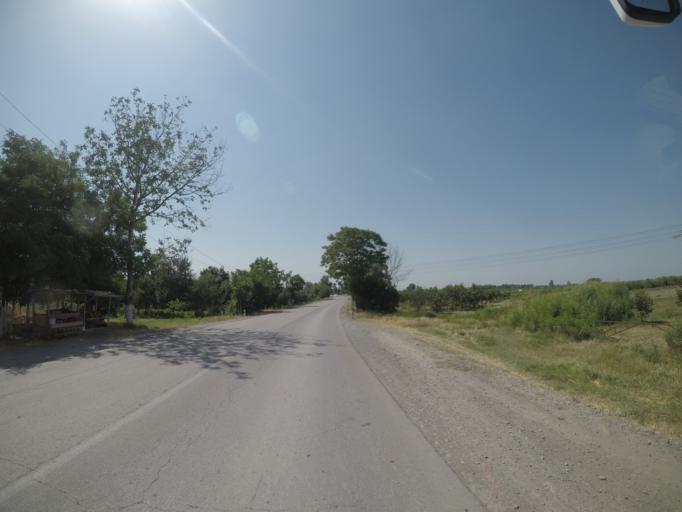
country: AZ
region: Agdas
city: Agdas
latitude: 40.7026
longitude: 47.5412
